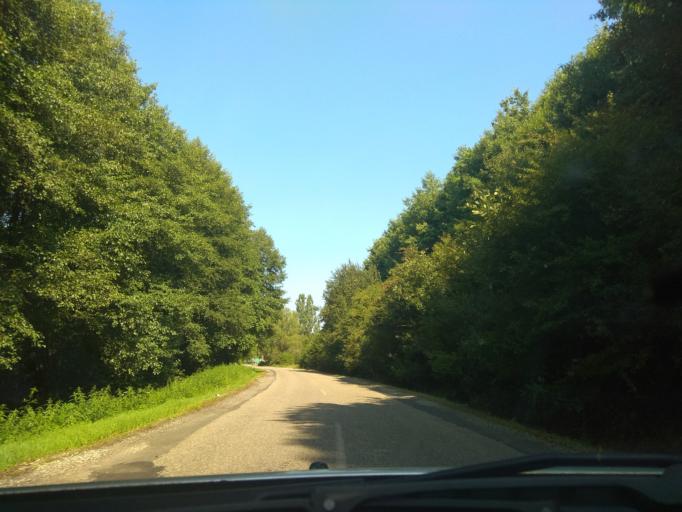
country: HU
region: Borsod-Abauj-Zemplen
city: Harsany
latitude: 47.9970
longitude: 20.7608
